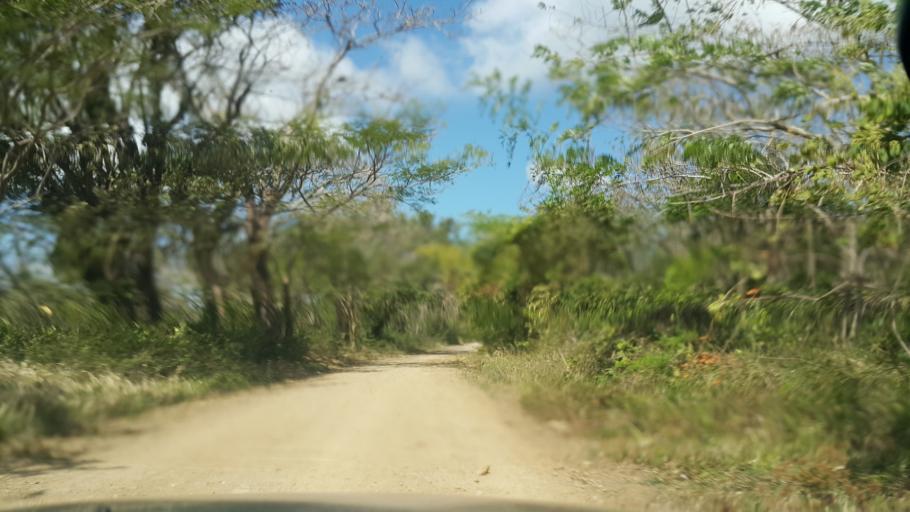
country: NI
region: Rivas
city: San Juan del Sur
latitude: 11.3100
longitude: -85.8423
